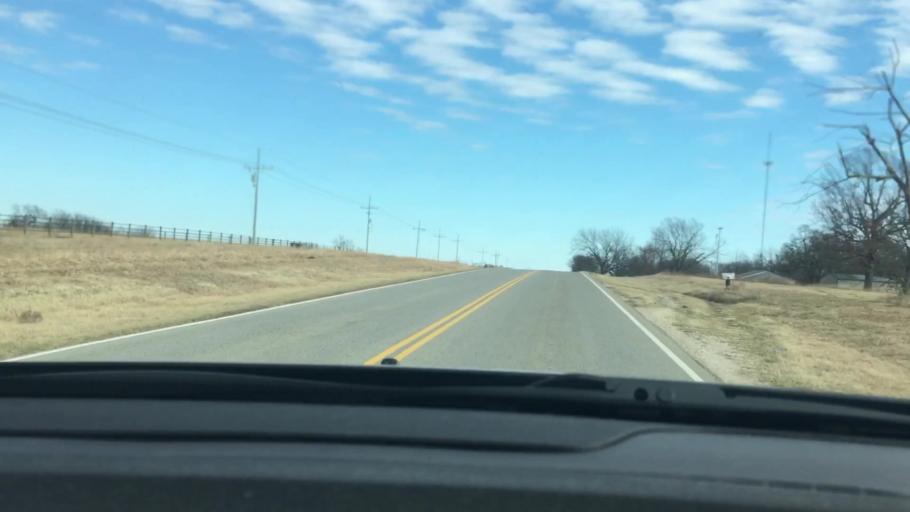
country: US
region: Oklahoma
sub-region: Garvin County
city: Stratford
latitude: 34.7968
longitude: -96.8517
